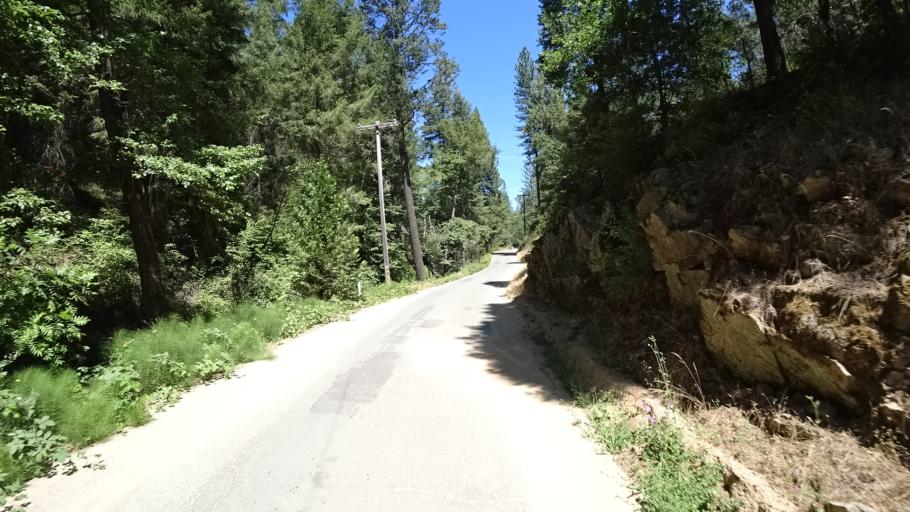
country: US
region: California
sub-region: Amador County
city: Pioneer
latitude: 38.4092
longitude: -120.5235
